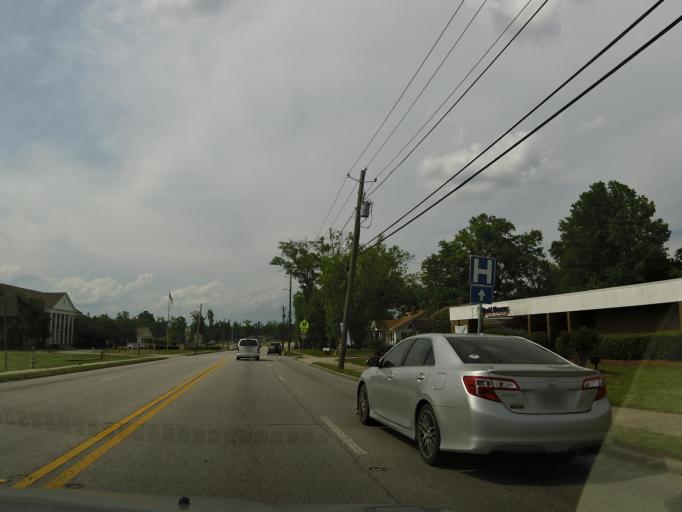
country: US
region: Georgia
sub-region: McDuffie County
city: Thomson
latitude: 33.4711
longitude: -82.5051
